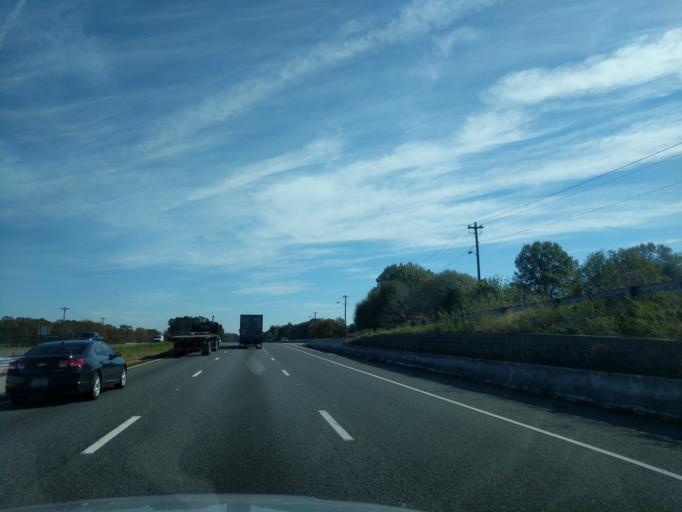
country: US
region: South Carolina
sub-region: Cherokee County
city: Gaffney
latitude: 35.0970
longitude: -81.6686
